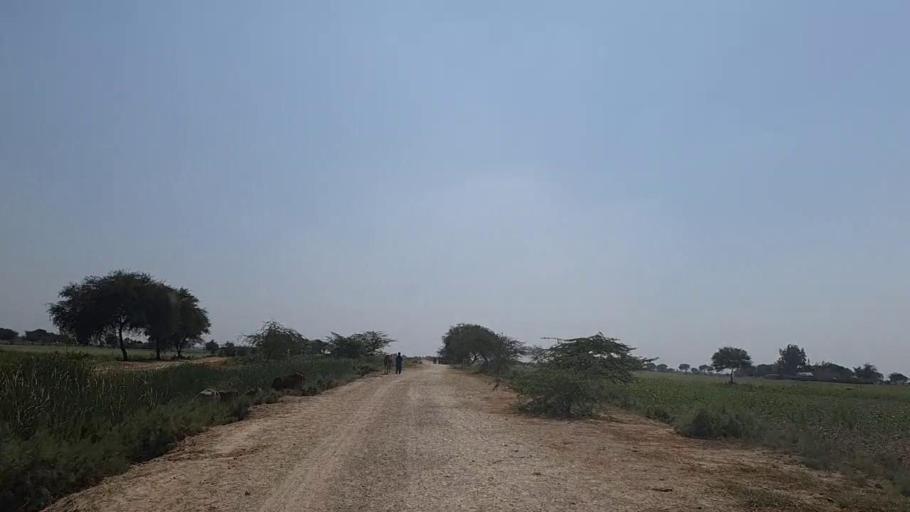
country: PK
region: Sindh
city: Mirpur Batoro
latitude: 24.5504
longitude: 68.3171
